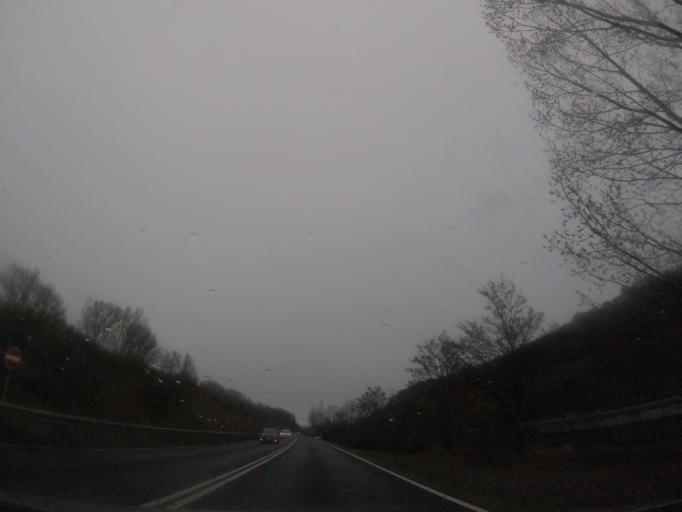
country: DE
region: Rheinland-Pfalz
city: Nackenheim
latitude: 49.9113
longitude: 8.3471
